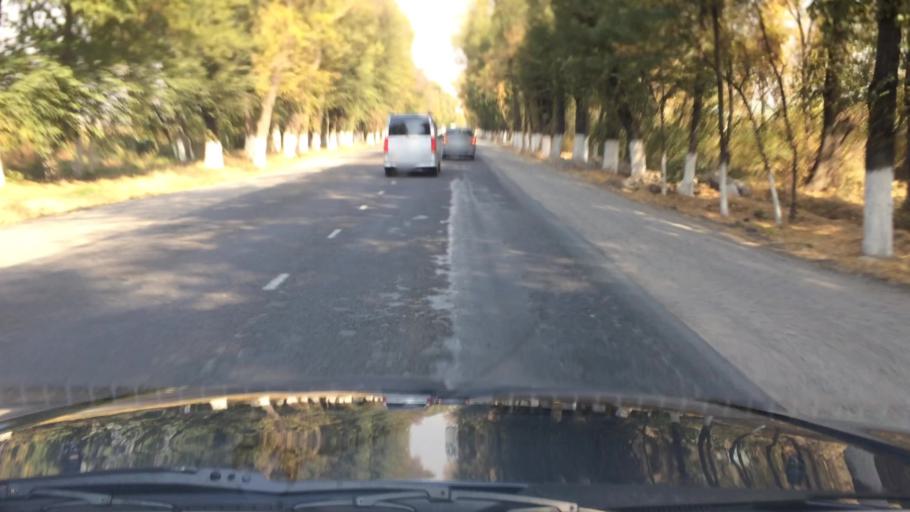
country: KG
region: Chuy
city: Lebedinovka
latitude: 42.9172
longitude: 74.6889
